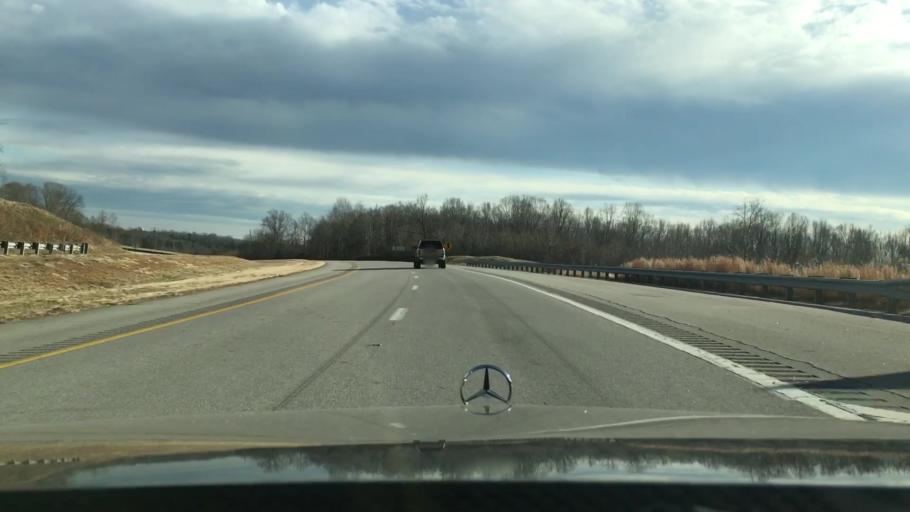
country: US
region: Virginia
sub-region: City of Danville
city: Danville
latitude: 36.6151
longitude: -79.3645
